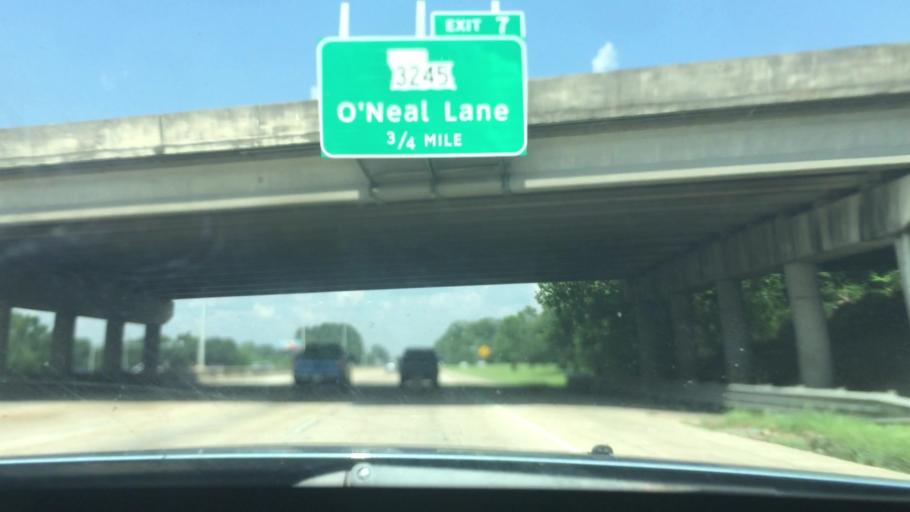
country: US
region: Louisiana
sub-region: East Baton Rouge Parish
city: Shenandoah
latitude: 30.4380
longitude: -91.0246
